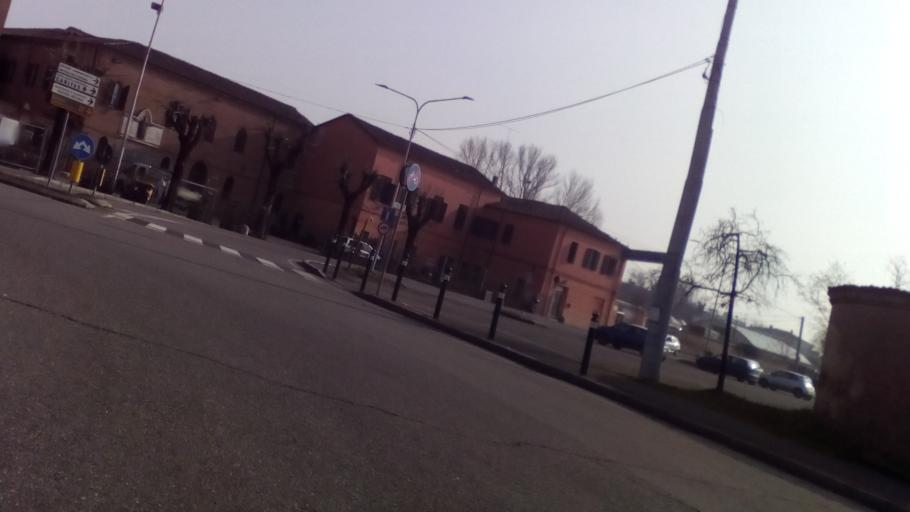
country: IT
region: Emilia-Romagna
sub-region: Provincia di Modena
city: Modena
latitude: 44.6600
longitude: 10.9106
